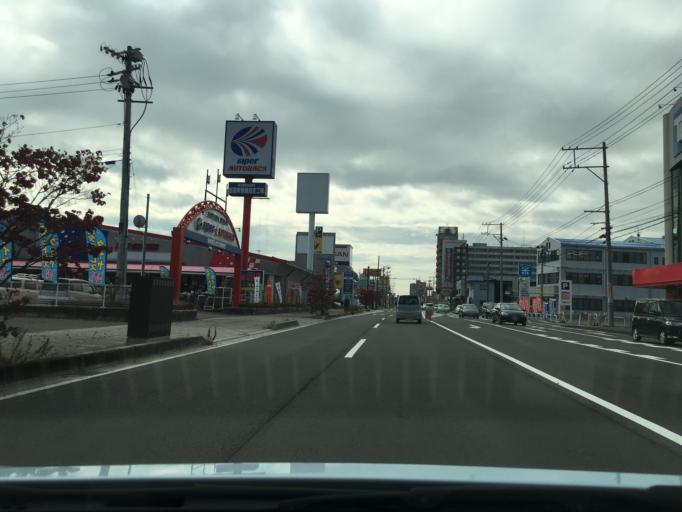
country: JP
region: Fukushima
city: Koriyama
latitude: 37.3683
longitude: 140.3709
